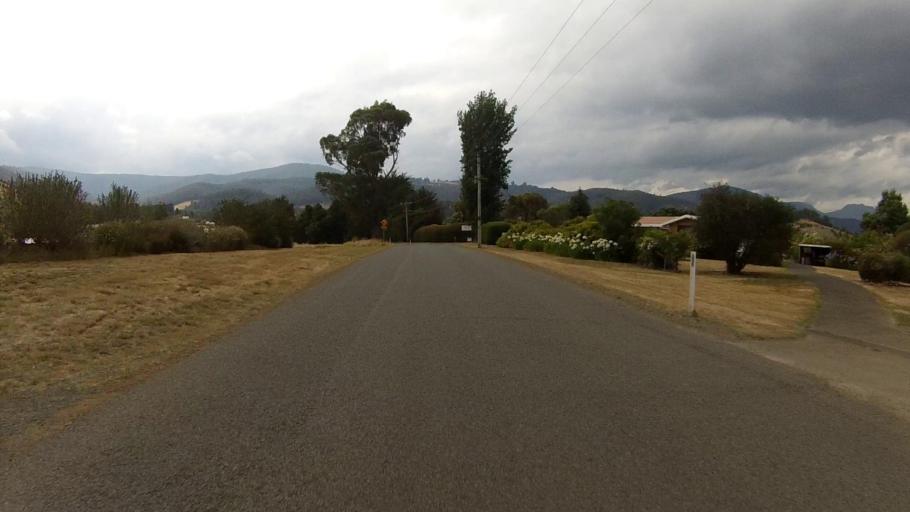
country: AU
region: Tasmania
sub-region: Huon Valley
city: Huonville
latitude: -42.9881
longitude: 147.0610
